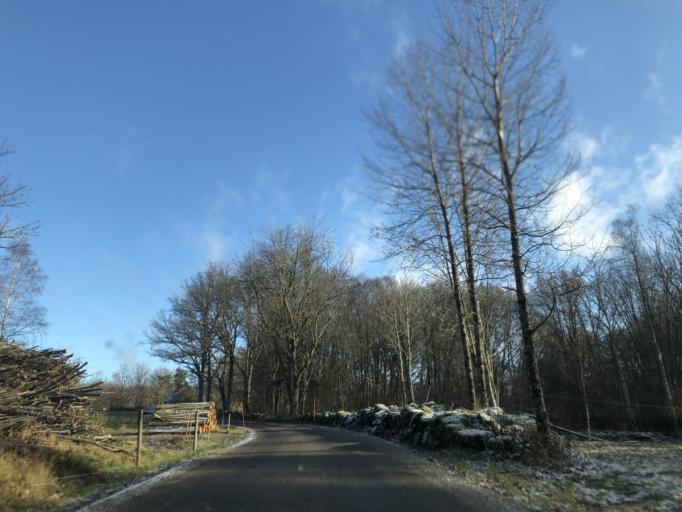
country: SE
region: Vaestra Goetaland
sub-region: Ulricehamns Kommun
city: Ulricehamn
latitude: 57.7261
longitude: 13.4141
